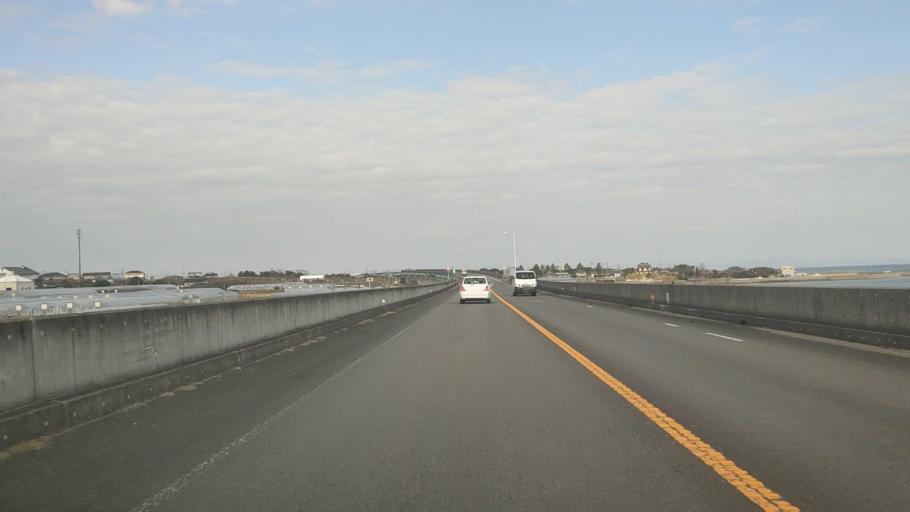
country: JP
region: Nagasaki
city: Shimabara
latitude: 32.7334
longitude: 130.3683
